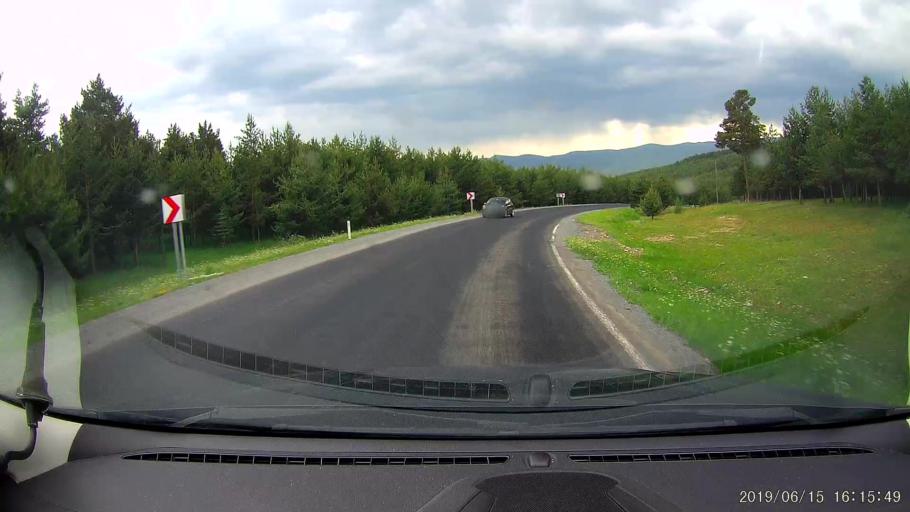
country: TR
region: Ardahan
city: Hanak
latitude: 41.2639
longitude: 42.8565
